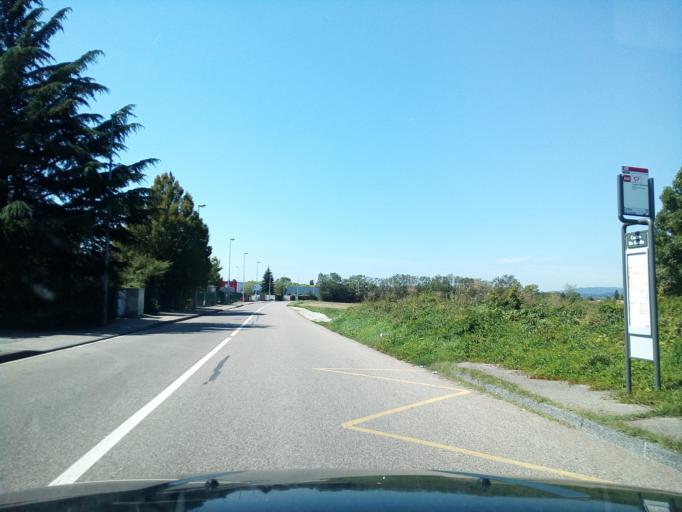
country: FR
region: Rhone-Alpes
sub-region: Departement du Rhone
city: Vaulx-en-Velin
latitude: 45.7833
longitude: 4.9409
